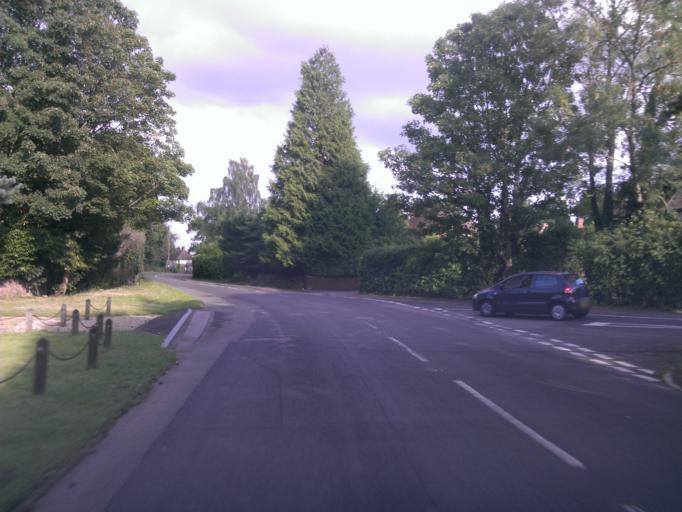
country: GB
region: England
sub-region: Kent
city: Sevenoaks
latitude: 51.1958
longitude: 0.2004
